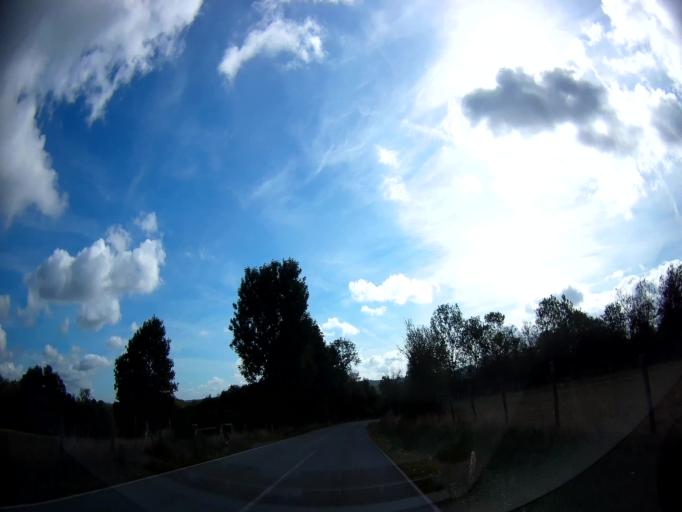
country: BE
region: Wallonia
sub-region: Province du Luxembourg
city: Wellin
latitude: 50.1733
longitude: 5.1243
